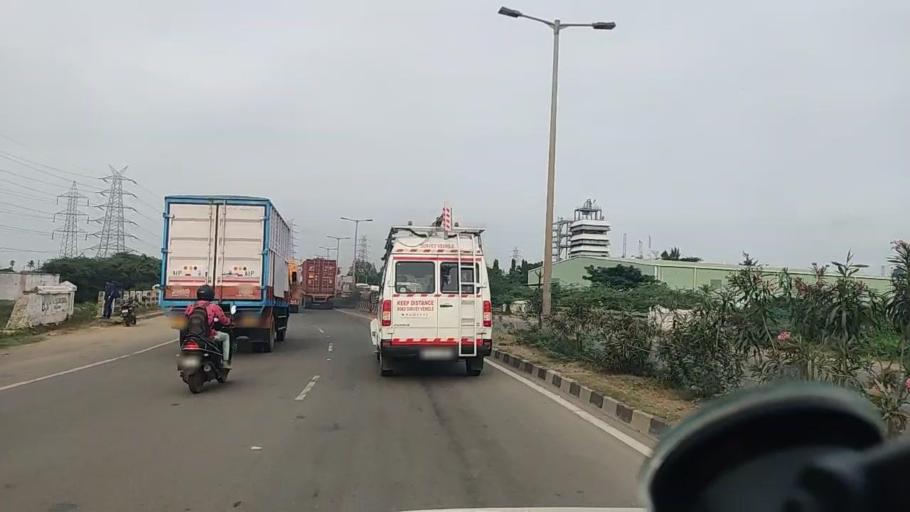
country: IN
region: Tamil Nadu
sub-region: Thiruvallur
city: Manali
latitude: 13.1798
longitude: 80.2557
